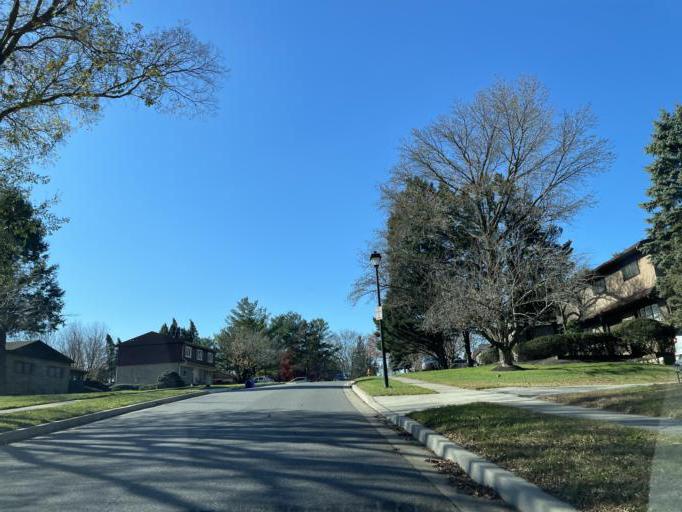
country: US
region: Maryland
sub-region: Baltimore County
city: Mays Chapel
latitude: 39.3868
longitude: -76.6704
